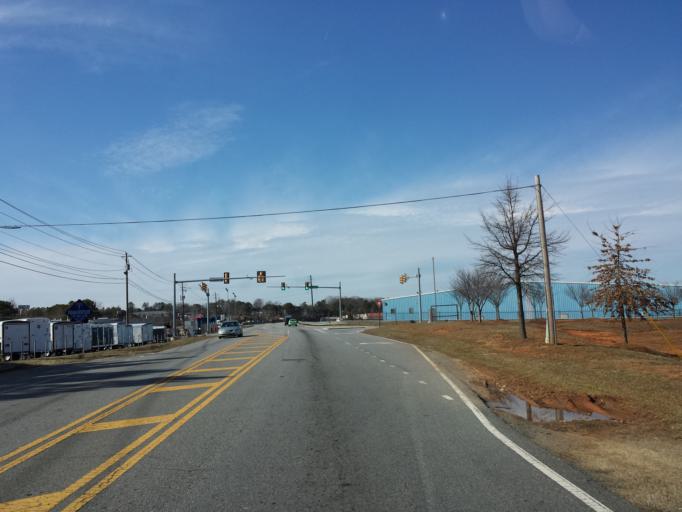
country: US
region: Georgia
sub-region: Cobb County
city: Kennesaw
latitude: 34.0098
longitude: -84.6056
